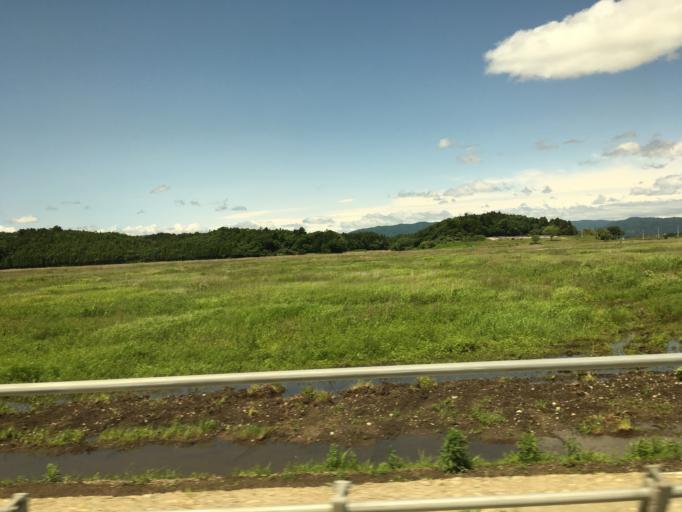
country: JP
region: Fukushima
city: Namie
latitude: 37.4794
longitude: 141.0294
